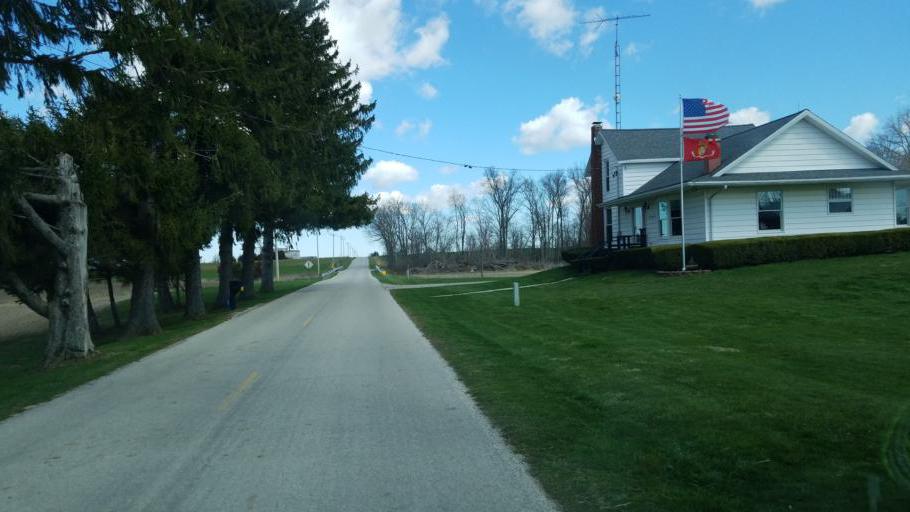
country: US
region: Ohio
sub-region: Sandusky County
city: Mount Carmel
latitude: 41.1260
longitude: -82.9384
